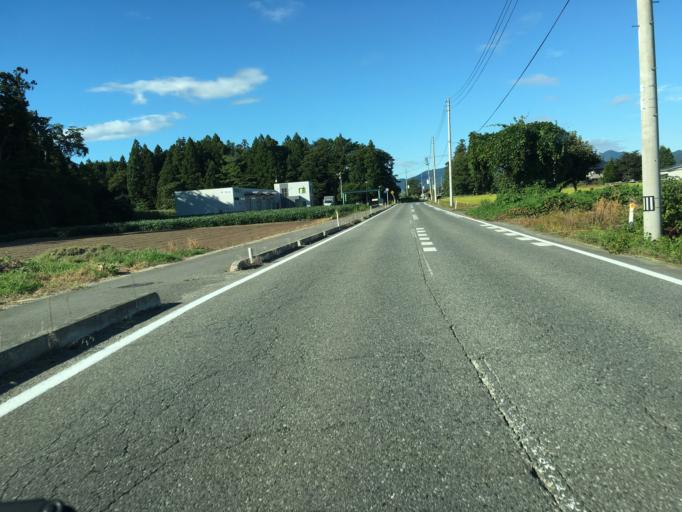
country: JP
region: Yamagata
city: Takahata
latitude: 37.9799
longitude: 140.1555
